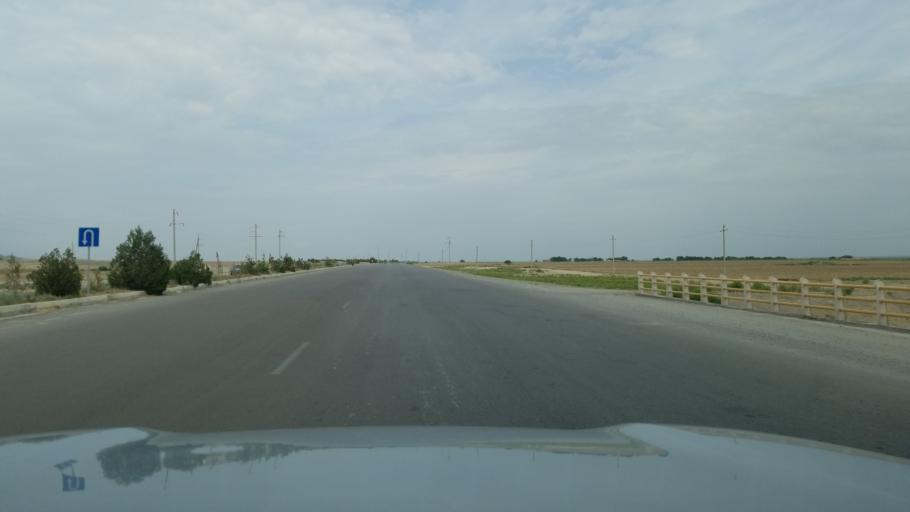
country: TM
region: Ahal
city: Baharly
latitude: 38.2230
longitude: 57.7980
